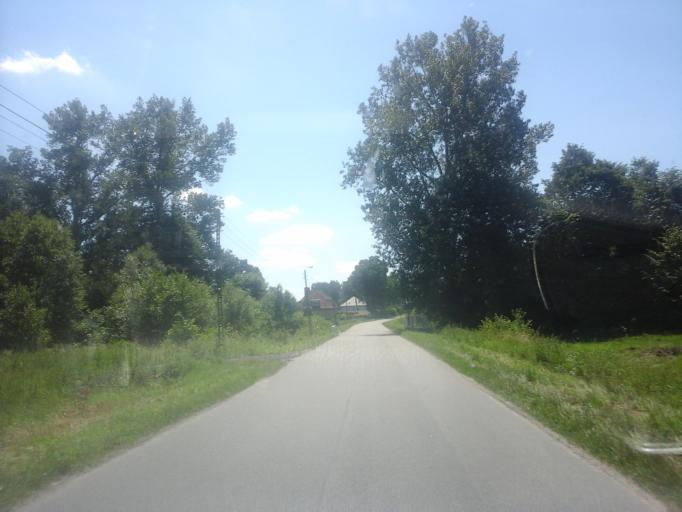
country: PL
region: West Pomeranian Voivodeship
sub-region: Powiat bialogardzki
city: Bialogard
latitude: 54.0510
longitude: 16.0192
